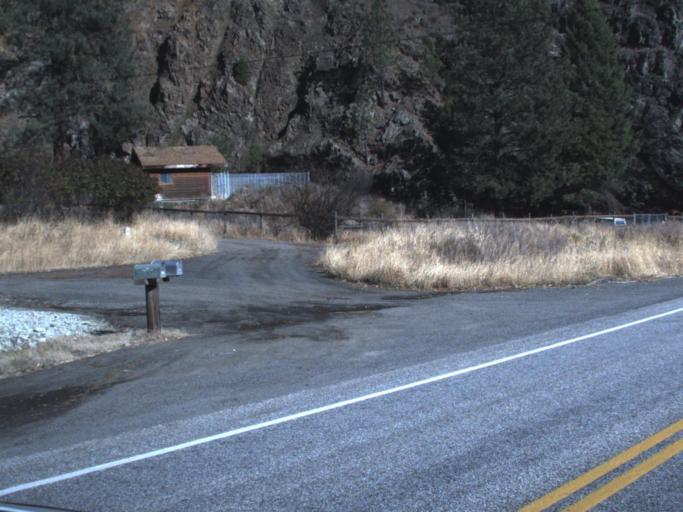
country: US
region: Washington
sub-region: Ferry County
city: Republic
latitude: 48.6513
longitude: -118.7062
